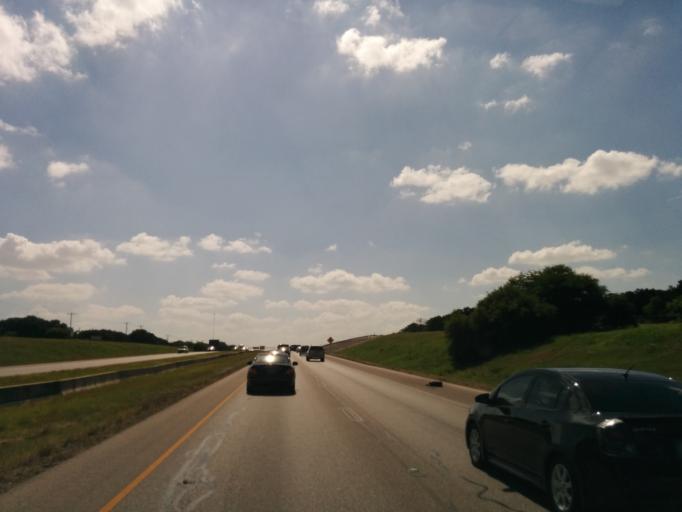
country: US
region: Texas
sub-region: Bexar County
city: Live Oak
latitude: 29.6029
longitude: -98.3683
